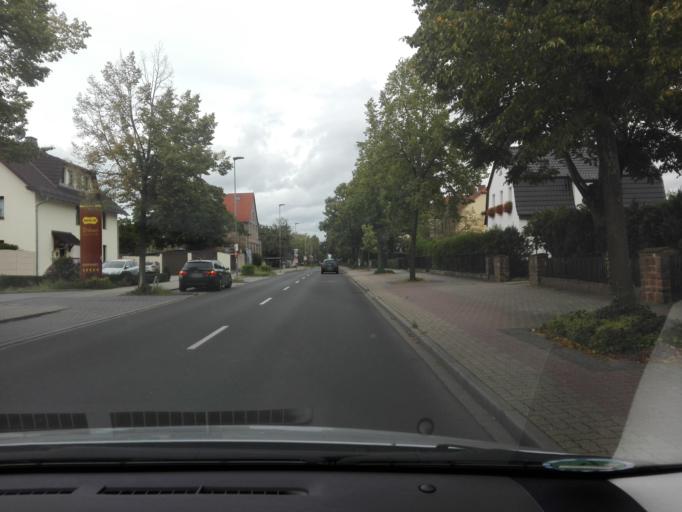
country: DE
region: Saxony-Anhalt
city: Merseburg
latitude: 51.3685
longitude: 11.9900
